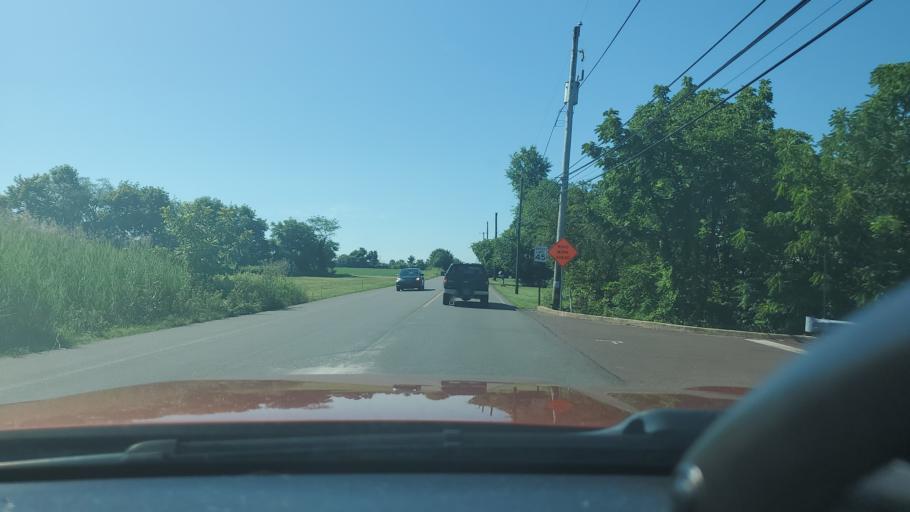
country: US
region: Pennsylvania
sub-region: Montgomery County
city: Limerick
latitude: 40.2392
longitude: -75.5277
